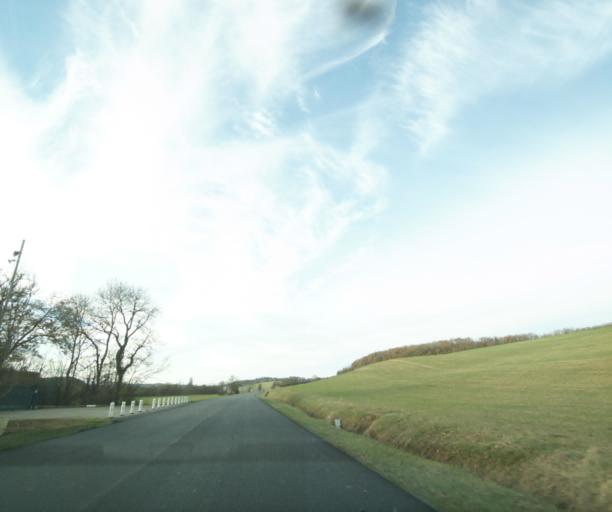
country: FR
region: Midi-Pyrenees
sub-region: Departement du Gers
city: Jegun
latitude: 43.6852
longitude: 0.4884
